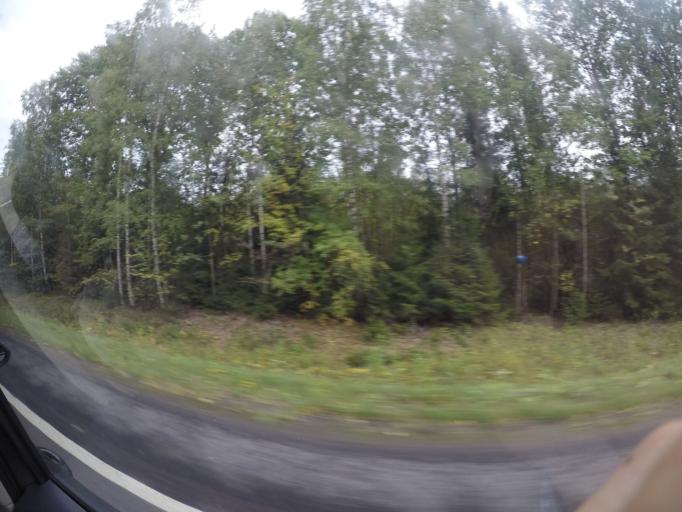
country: FI
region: Haeme
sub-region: Haemeenlinna
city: Parola
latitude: 61.1047
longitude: 24.4097
